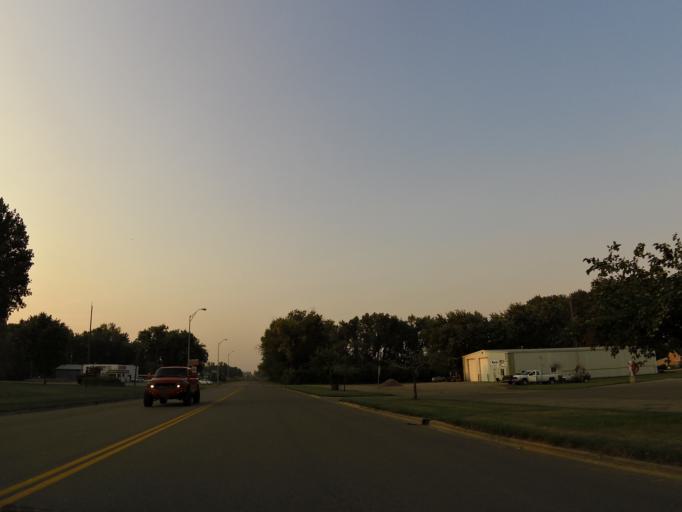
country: US
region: North Dakota
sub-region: Grand Forks County
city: Larimore
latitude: 47.9099
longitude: -97.6237
